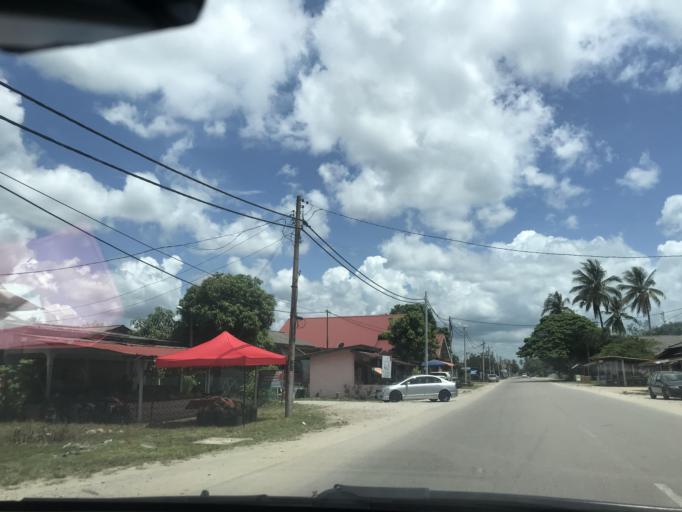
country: TH
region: Narathiwat
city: Tak Bai
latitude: 6.2270
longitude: 102.1011
